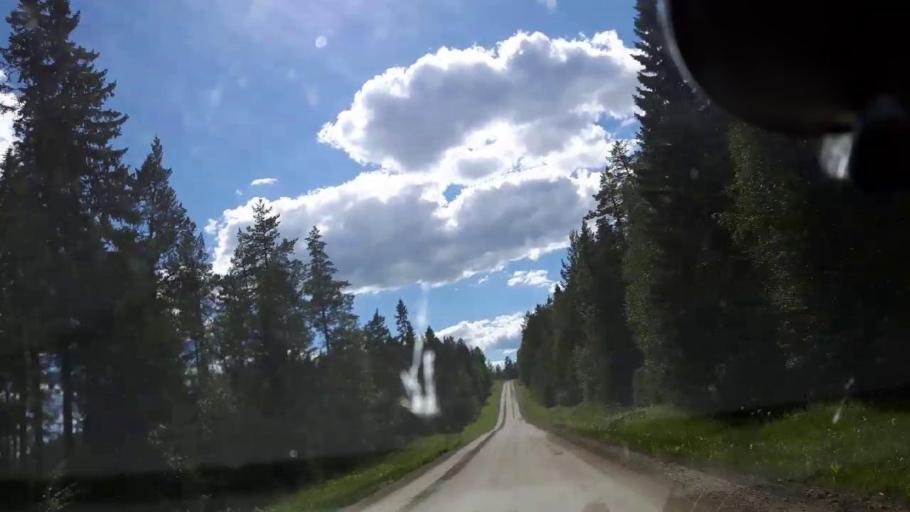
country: SE
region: Vaesternorrland
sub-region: Ange Kommun
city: Ange
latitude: 62.7210
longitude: 15.6360
